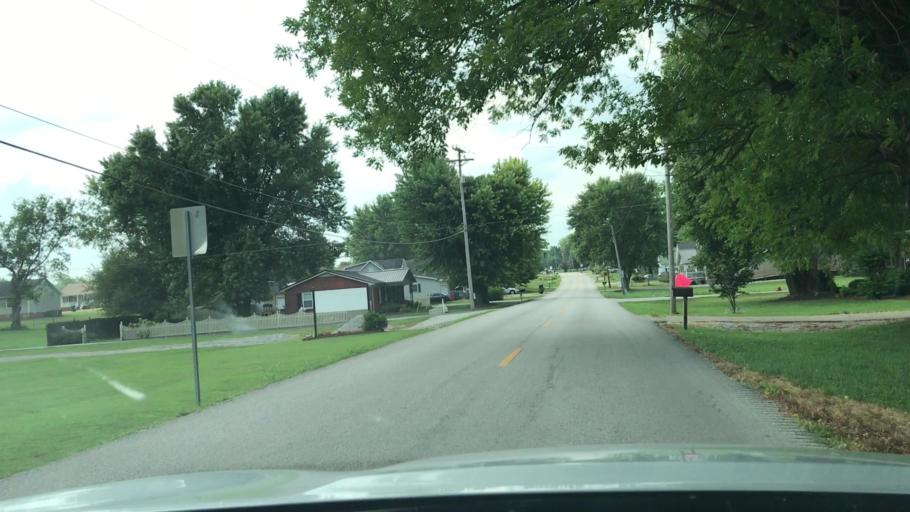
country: US
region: Kentucky
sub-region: Todd County
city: Elkton
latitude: 36.8060
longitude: -87.1482
